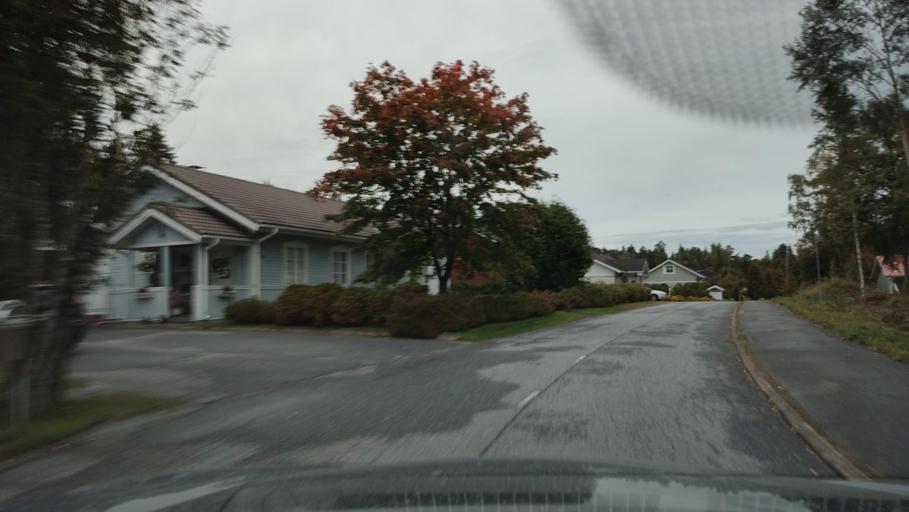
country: FI
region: Ostrobothnia
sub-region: Sydosterbotten
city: Kristinestad
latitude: 62.2796
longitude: 21.3516
